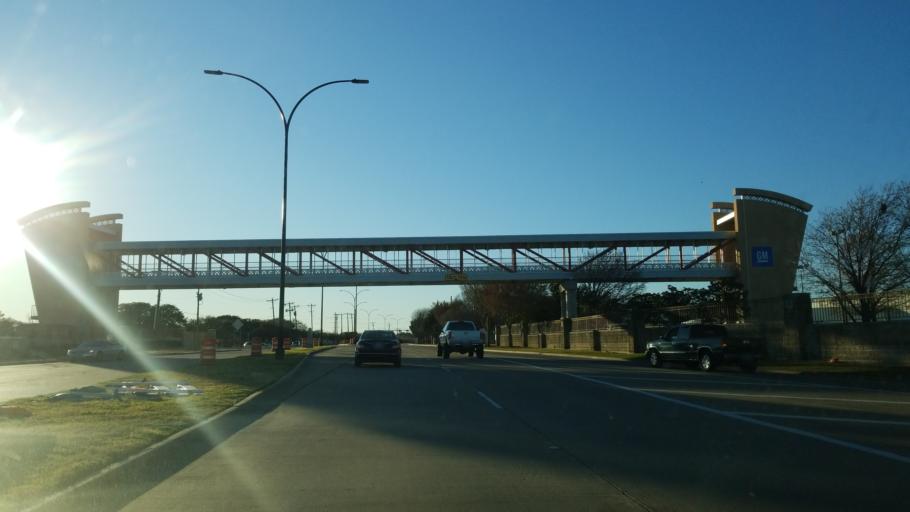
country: US
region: Texas
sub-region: Tarrant County
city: Arlington
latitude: 32.7358
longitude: -97.0645
